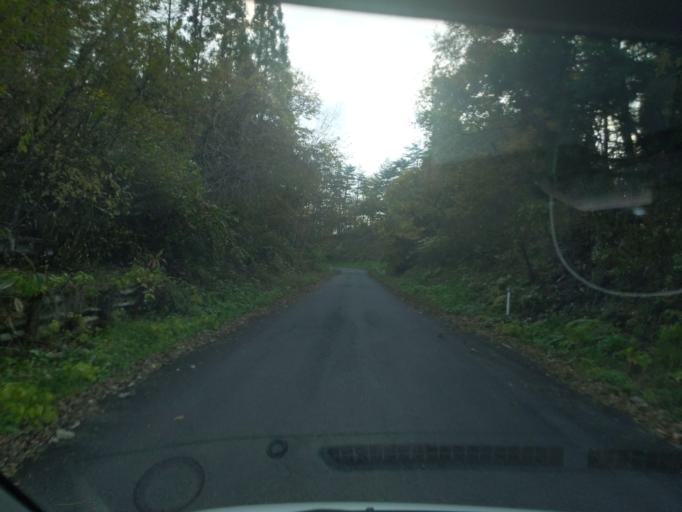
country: JP
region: Iwate
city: Ichinoseki
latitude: 38.9996
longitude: 141.0052
